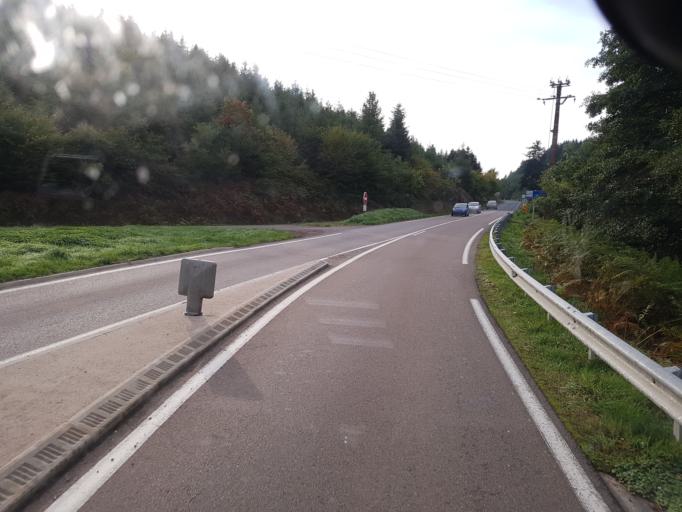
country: FR
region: Bourgogne
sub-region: Departement de Saone-et-Loire
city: Chauffailles
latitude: 46.2694
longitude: 4.3960
